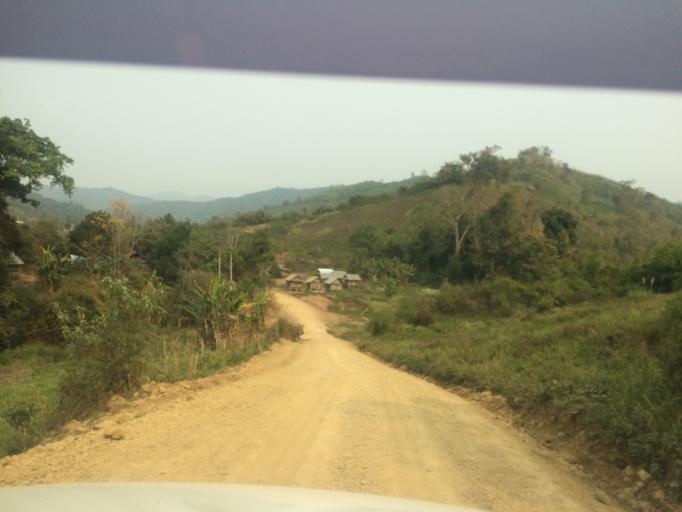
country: LA
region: Loungnamtha
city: Muang Nale
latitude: 20.4389
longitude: 101.7182
